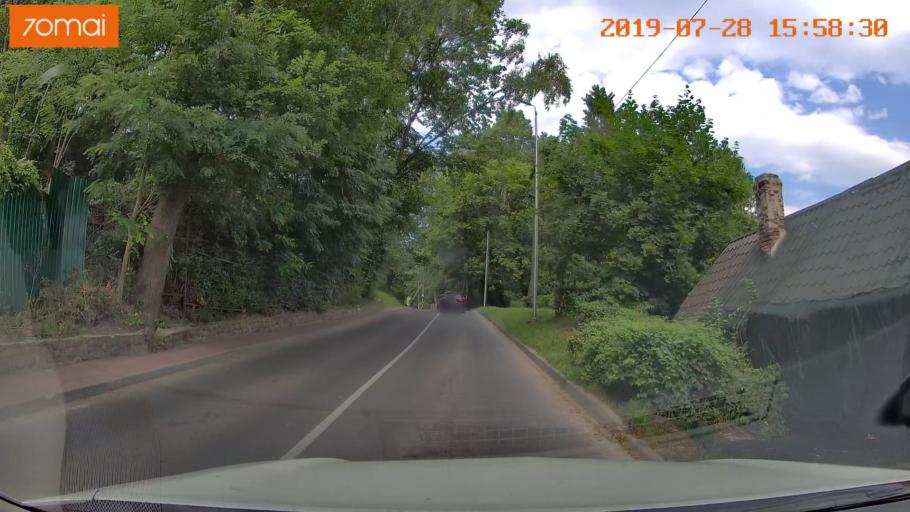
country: RU
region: Kaliningrad
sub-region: Gorod Svetlogorsk
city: Svetlogorsk
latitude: 54.9396
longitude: 20.1614
